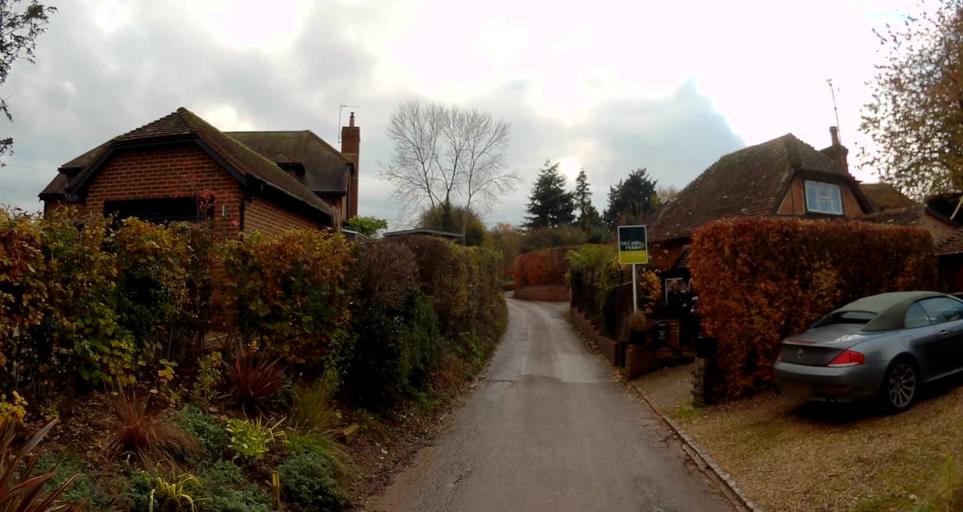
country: GB
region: England
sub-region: Hampshire
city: Long Sutton
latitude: 51.2208
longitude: -0.9444
